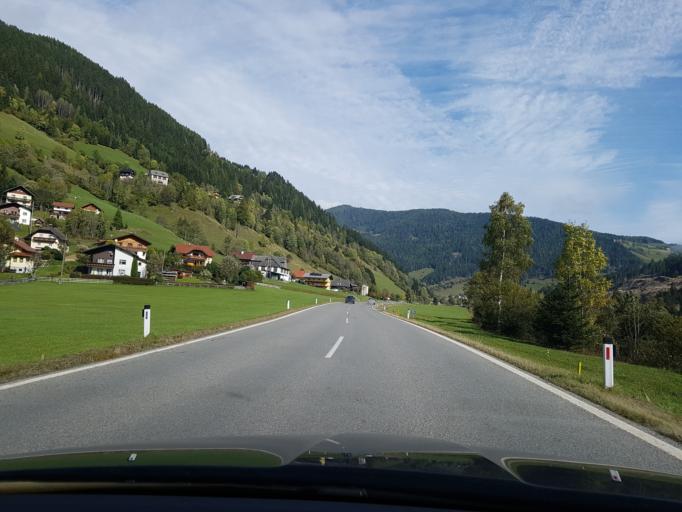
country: AT
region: Carinthia
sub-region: Politischer Bezirk Spittal an der Drau
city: Kleinkirchheim
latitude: 46.8414
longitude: 13.8781
